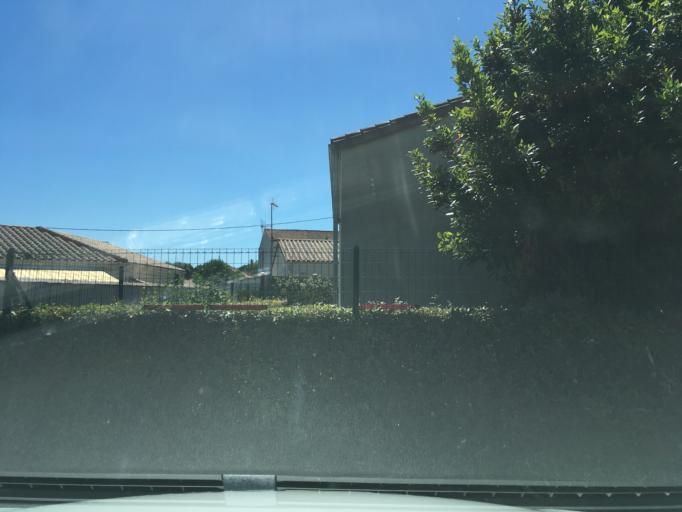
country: FR
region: Poitou-Charentes
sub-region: Departement des Deux-Sevres
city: Niort
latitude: 46.3261
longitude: -0.4301
